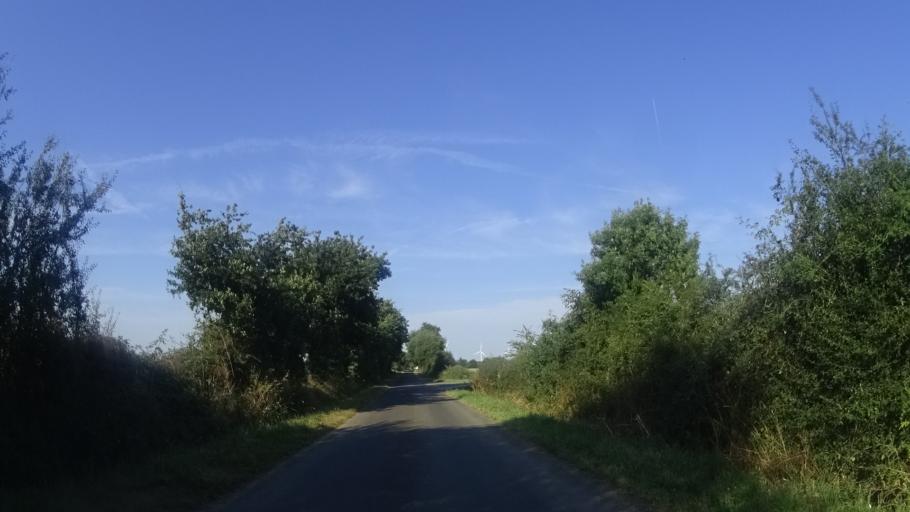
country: FR
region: Pays de la Loire
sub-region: Departement de la Loire-Atlantique
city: Joue-sur-Erdre
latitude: 47.4850
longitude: -1.3756
